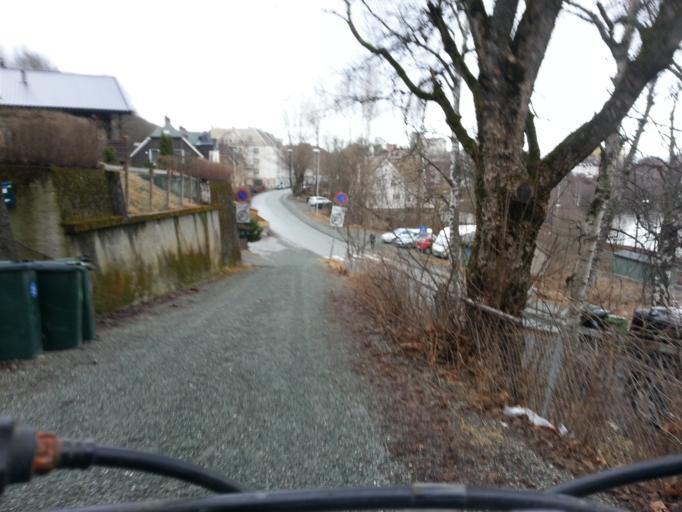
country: NO
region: Sor-Trondelag
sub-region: Trondheim
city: Trondheim
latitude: 63.4250
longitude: 10.3717
